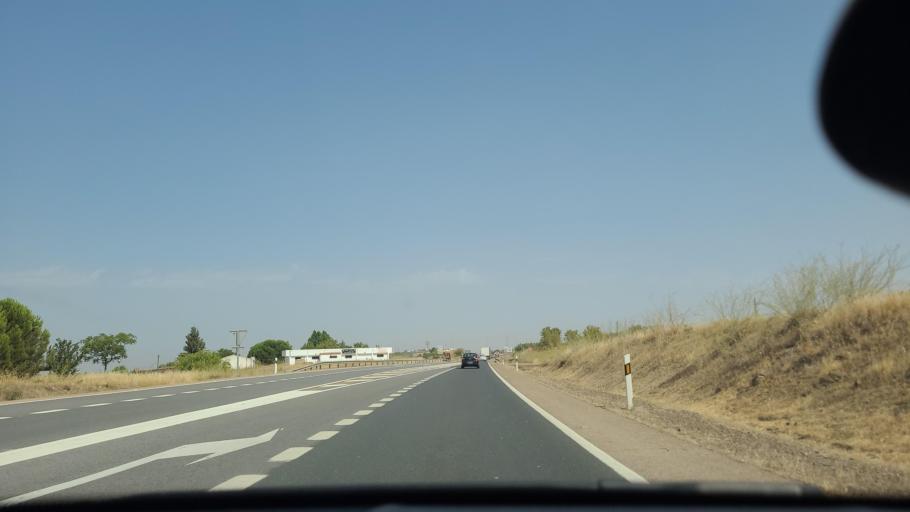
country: ES
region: Extremadura
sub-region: Provincia de Badajoz
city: Zafra
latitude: 38.4350
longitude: -6.4231
